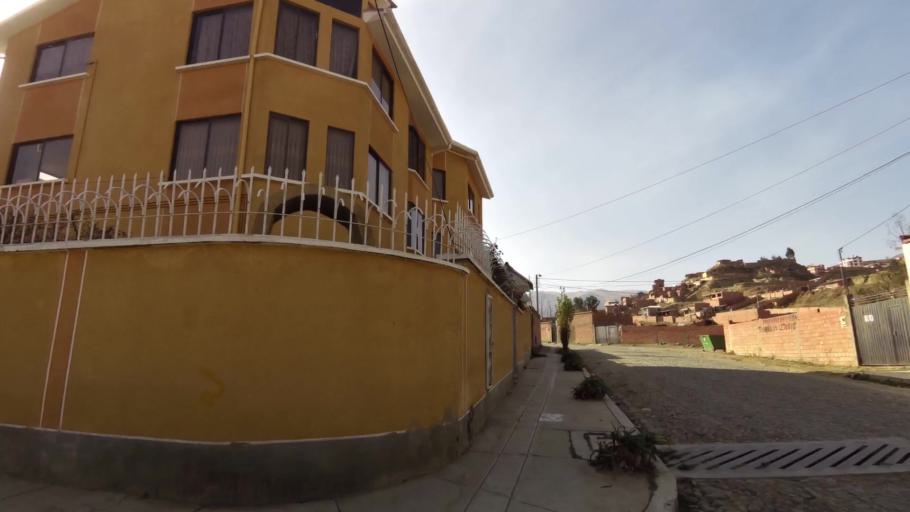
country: BO
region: La Paz
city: La Paz
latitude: -16.5178
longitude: -68.0824
